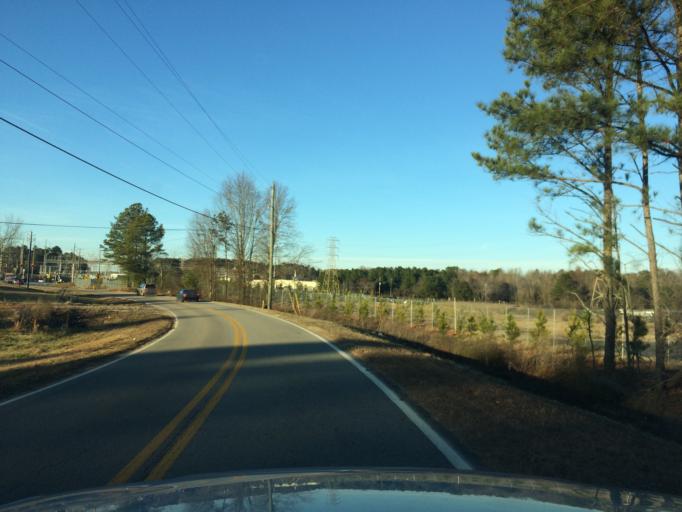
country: US
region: Georgia
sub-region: Barrow County
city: Winder
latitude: 33.9905
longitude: -83.7522
